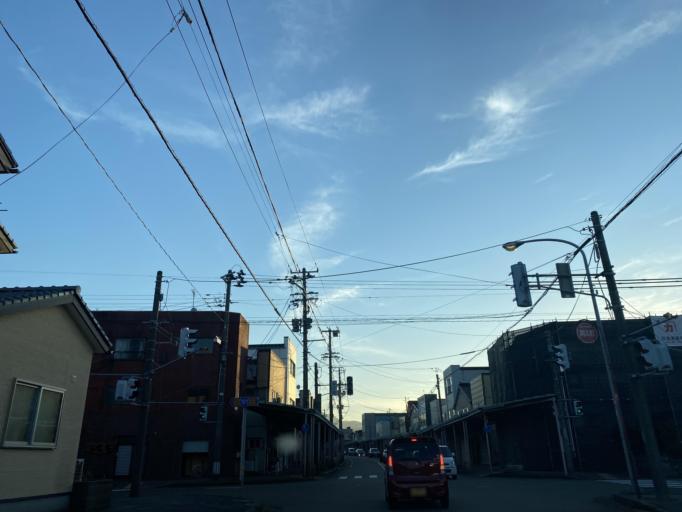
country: JP
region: Niigata
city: Kashiwazaki
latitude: 37.3748
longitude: 138.5634
